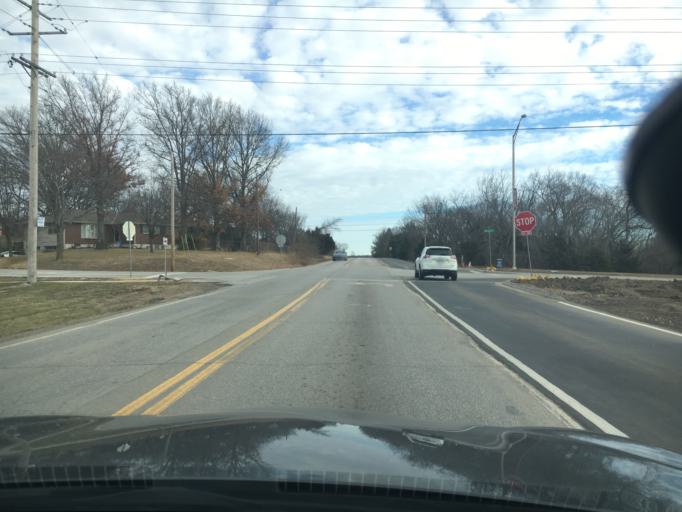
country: US
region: Missouri
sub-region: Jackson County
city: Grandview
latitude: 38.8547
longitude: -94.6310
